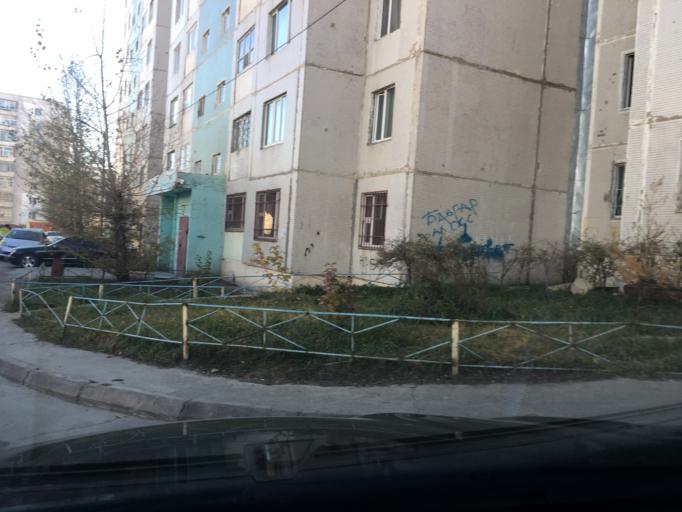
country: MN
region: Ulaanbaatar
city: Ulaanbaatar
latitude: 47.9277
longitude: 106.8802
